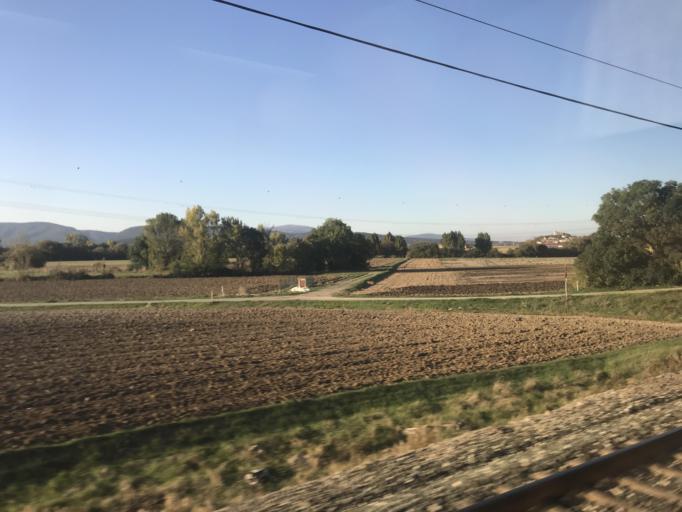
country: ES
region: Basque Country
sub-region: Provincia de Alava
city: Gasteiz / Vitoria
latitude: 42.8494
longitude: -2.7571
